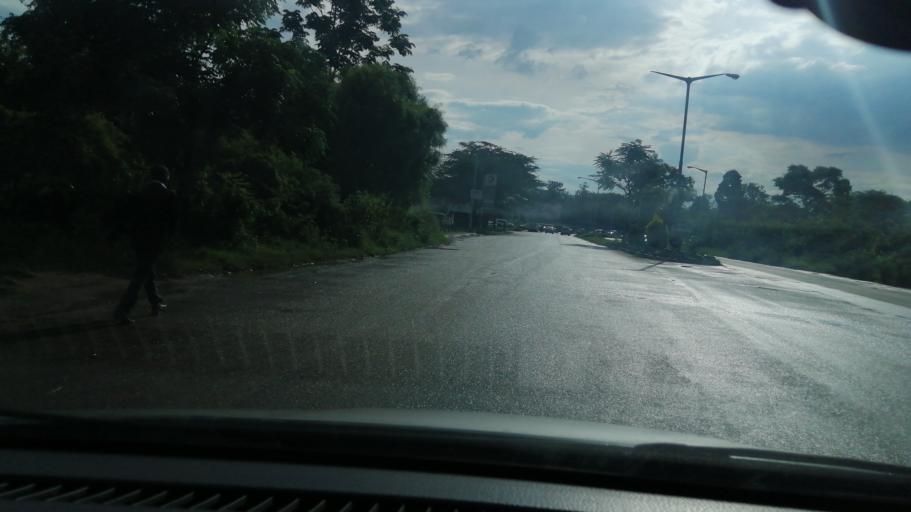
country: ZW
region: Harare
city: Harare
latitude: -17.7913
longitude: 31.0452
